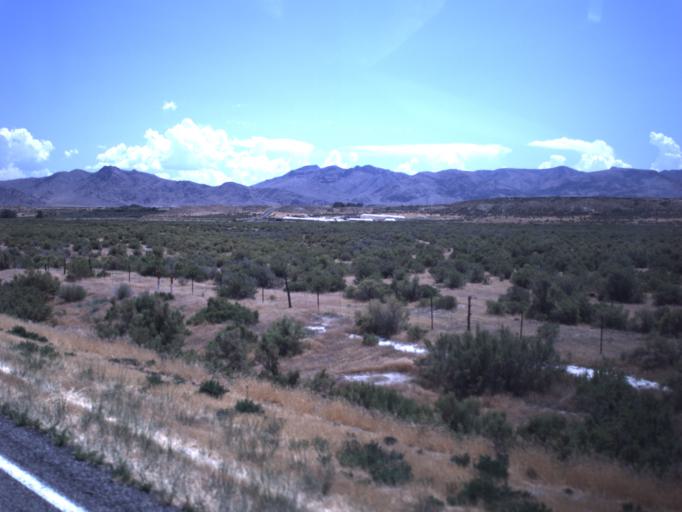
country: US
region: Utah
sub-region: Millard County
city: Delta
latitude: 39.5276
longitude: -112.3522
